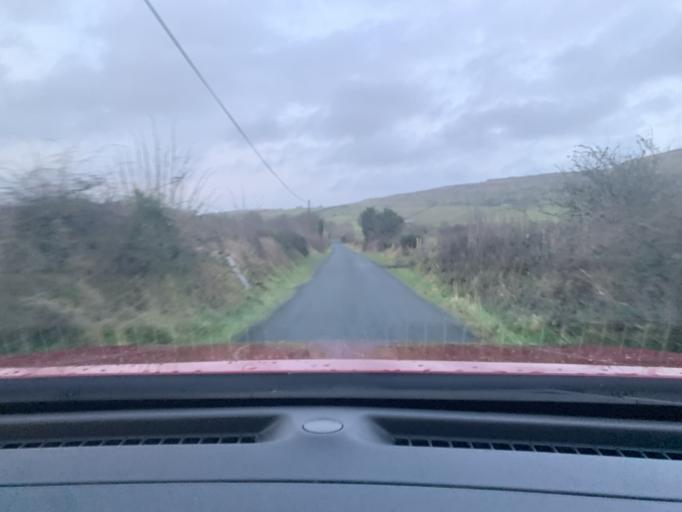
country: IE
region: Connaught
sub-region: Sligo
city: Ballymote
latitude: 54.0344
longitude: -8.4089
